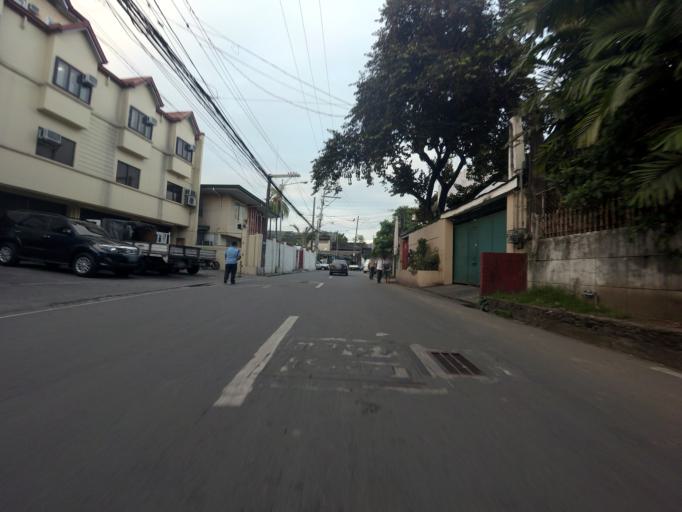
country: PH
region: Metro Manila
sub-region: San Juan
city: San Juan
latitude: 14.5977
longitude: 121.0325
